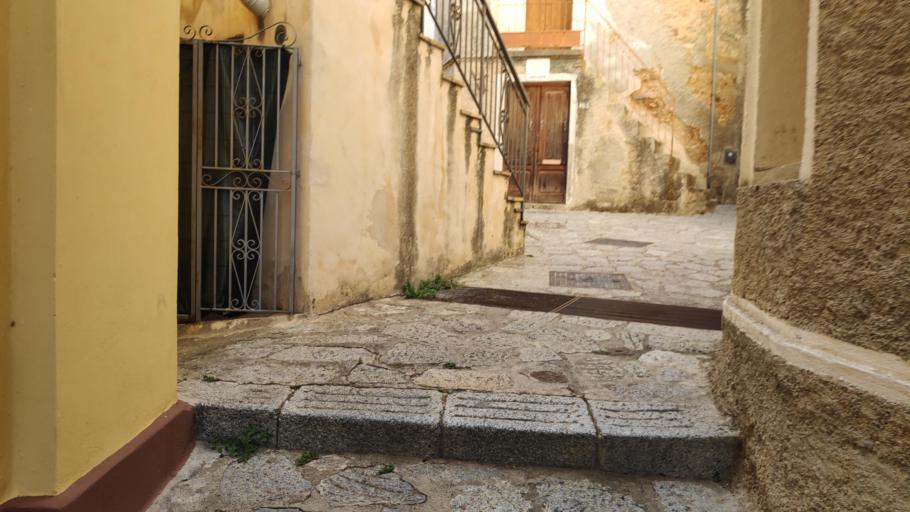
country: IT
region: Calabria
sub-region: Provincia di Catanzaro
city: Sant'Andrea Apostolo dello Ionio
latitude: 38.6213
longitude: 16.5298
